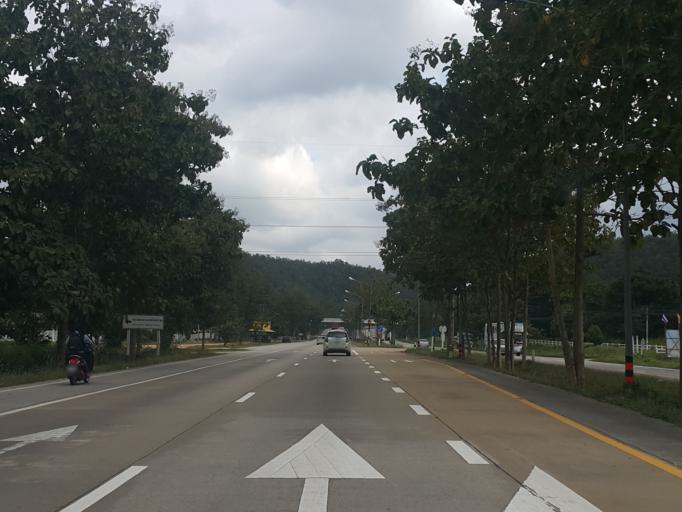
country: TH
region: Lamphun
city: Mae Tha
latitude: 18.4856
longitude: 99.1299
